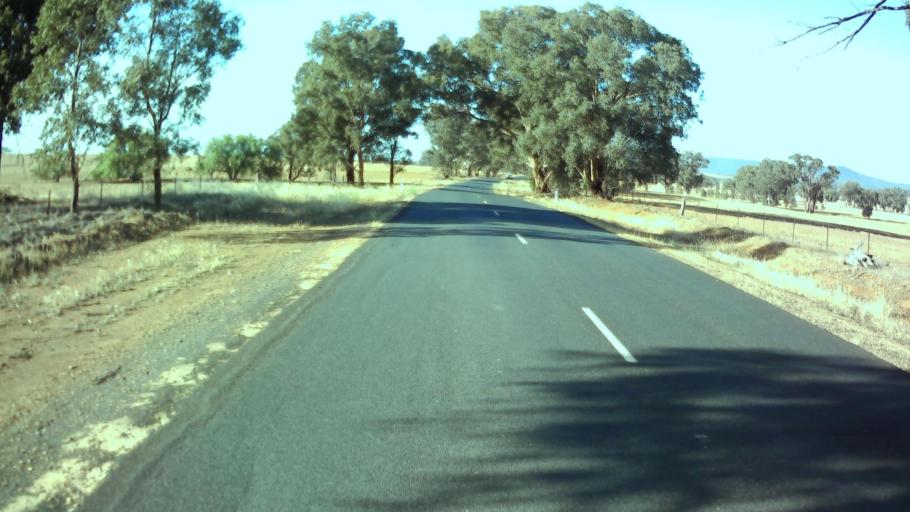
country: AU
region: New South Wales
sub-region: Weddin
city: Grenfell
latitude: -33.9166
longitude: 148.1422
